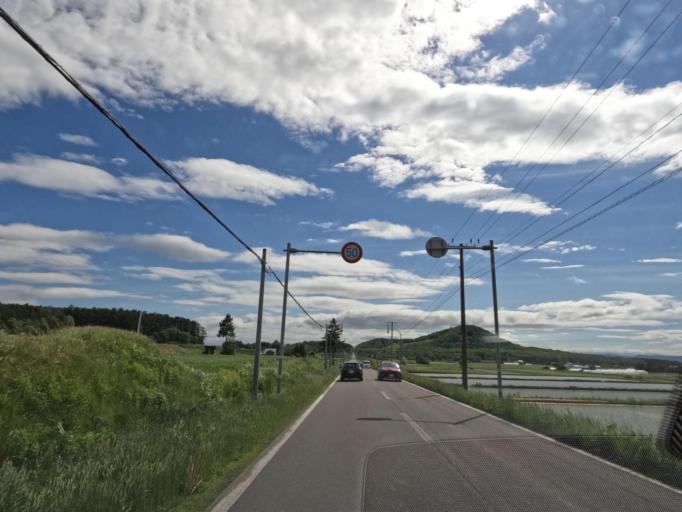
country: JP
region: Hokkaido
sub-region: Asahikawa-shi
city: Asahikawa
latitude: 43.8452
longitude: 142.5528
